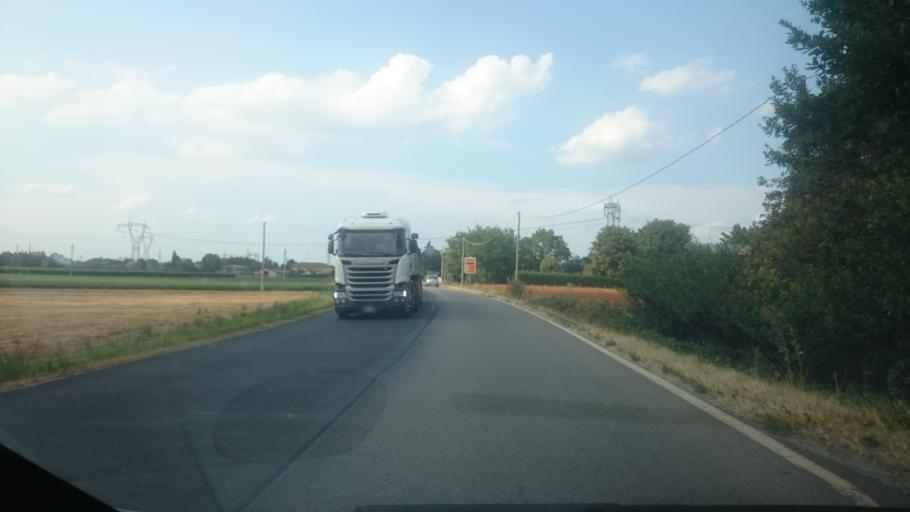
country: IT
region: Emilia-Romagna
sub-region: Provincia di Reggio Emilia
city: Salvaterra
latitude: 44.6163
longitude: 10.7787
